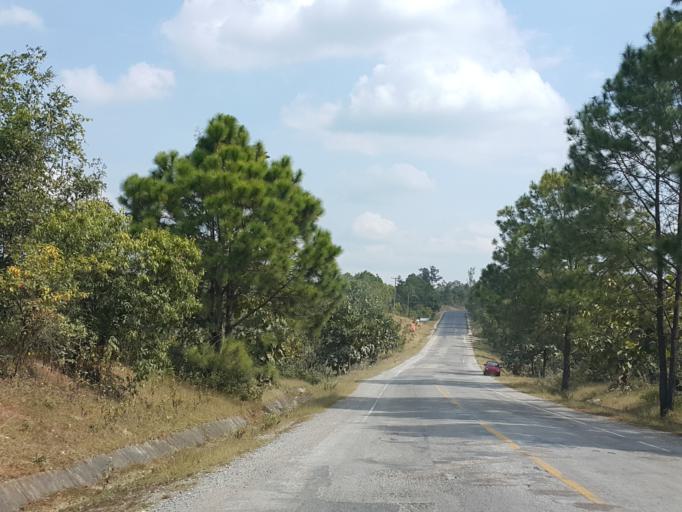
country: TH
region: Chiang Mai
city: Om Koi
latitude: 17.8207
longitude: 98.3613
